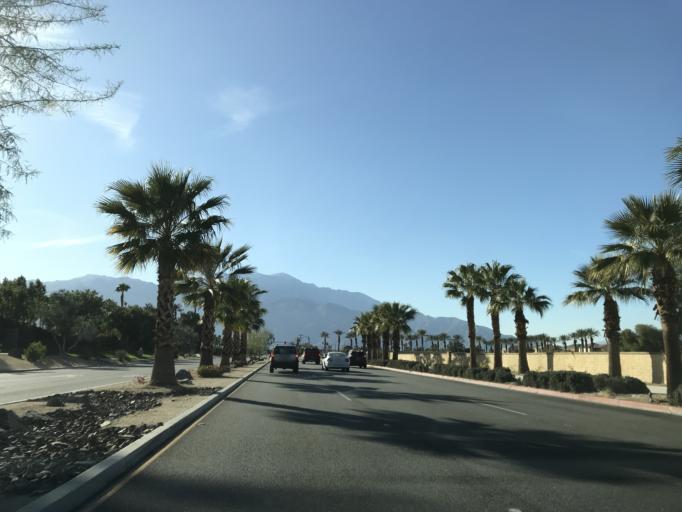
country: US
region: California
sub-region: Riverside County
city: Cathedral City
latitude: 33.8160
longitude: -116.4454
